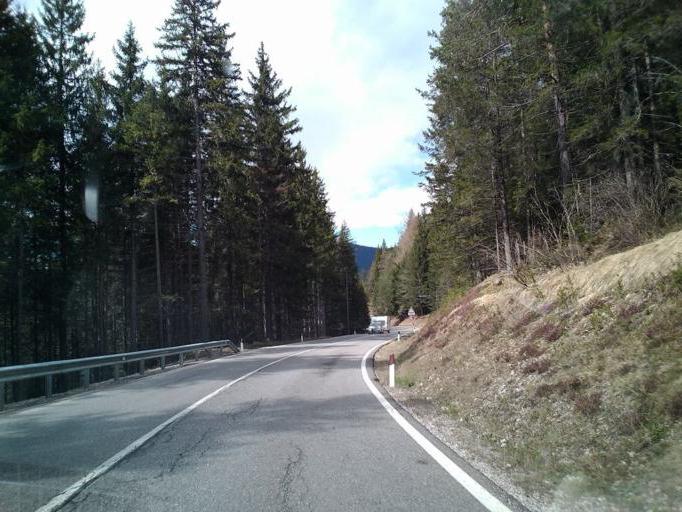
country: IT
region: Trentino-Alto Adige
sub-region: Bolzano
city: Dobbiaco
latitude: 46.7118
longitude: 12.2239
